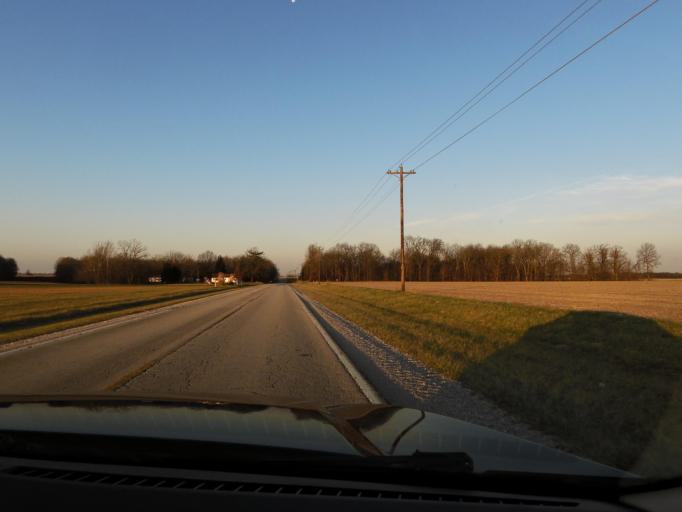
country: US
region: Illinois
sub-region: Marion County
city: Salem
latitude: 38.7653
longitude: -88.9785
